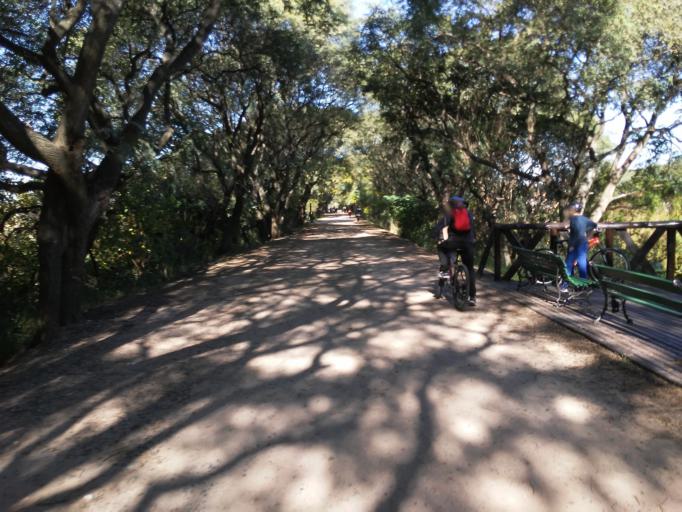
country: AR
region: Buenos Aires F.D.
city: Buenos Aires
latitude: -34.6122
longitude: -58.3565
